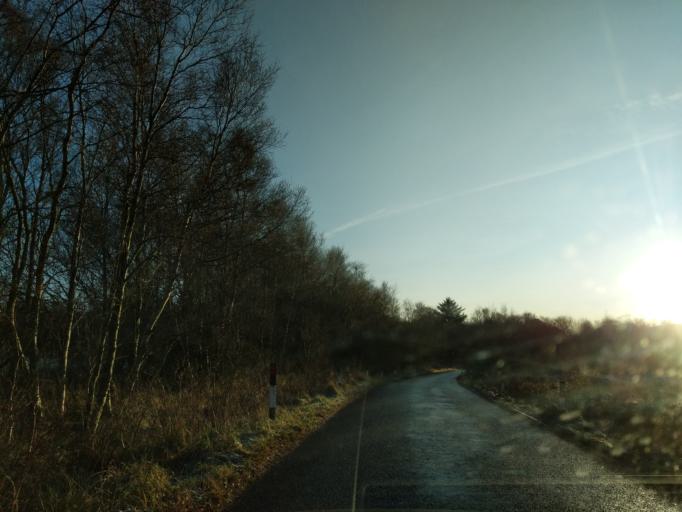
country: GB
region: Scotland
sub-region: Edinburgh
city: Balerno
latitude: 55.8619
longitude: -3.3331
